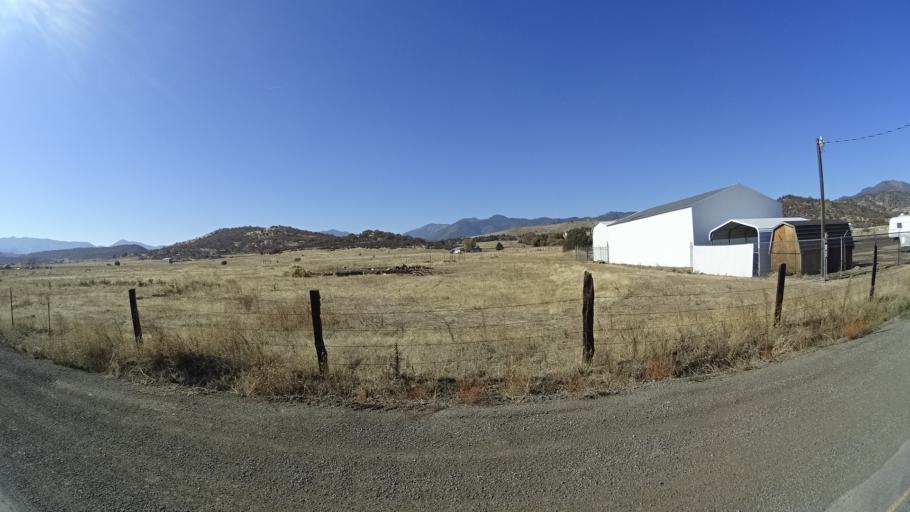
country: US
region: California
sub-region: Siskiyou County
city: Yreka
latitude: 41.7412
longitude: -122.5933
